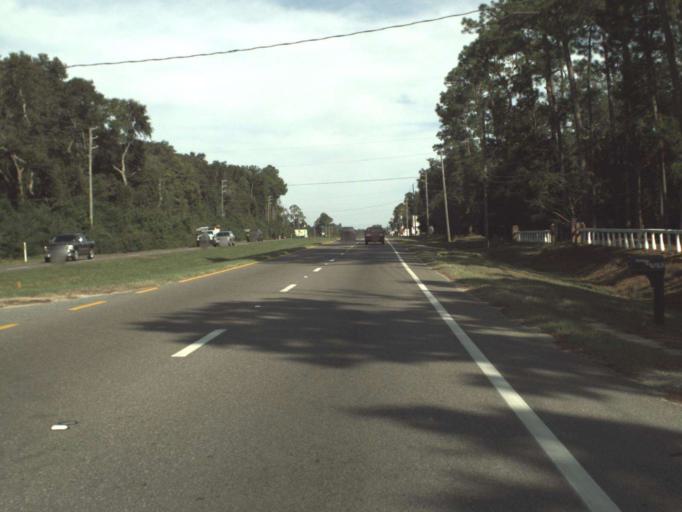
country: US
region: Florida
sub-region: Escambia County
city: Bellview
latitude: 30.4923
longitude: -87.3061
